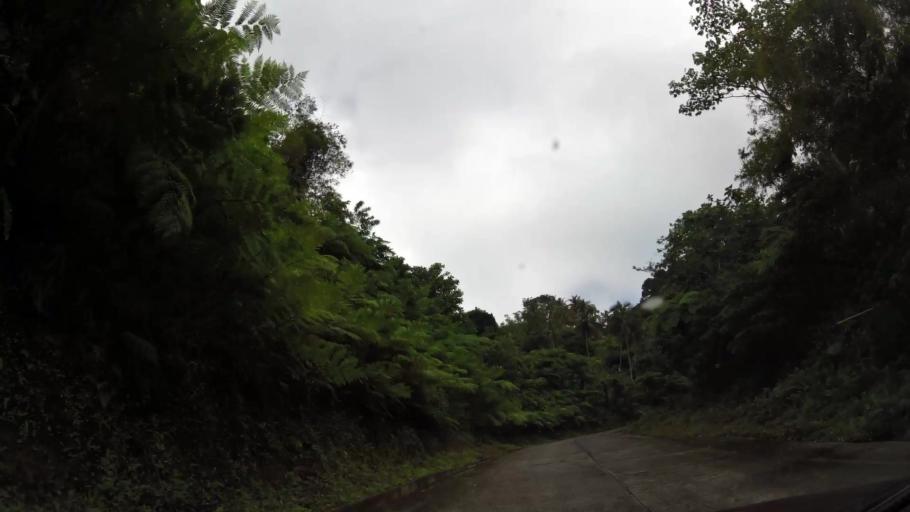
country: DM
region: Saint John
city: Portsmouth
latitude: 15.6133
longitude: -61.4460
